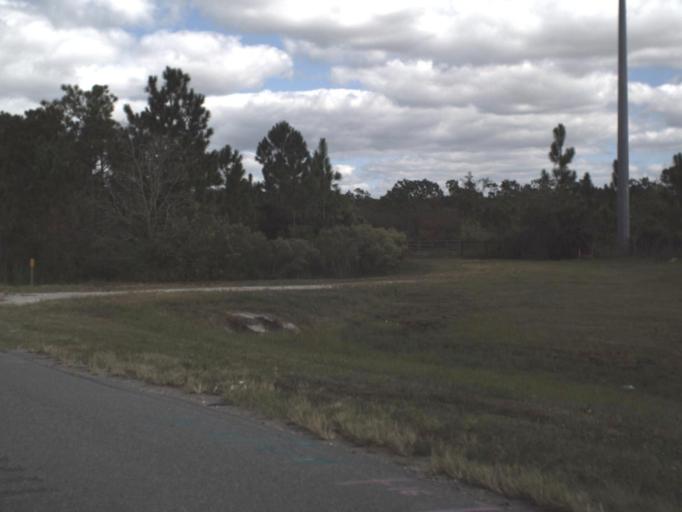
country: US
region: Florida
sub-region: Orange County
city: Southchase
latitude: 28.3737
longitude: -81.3901
